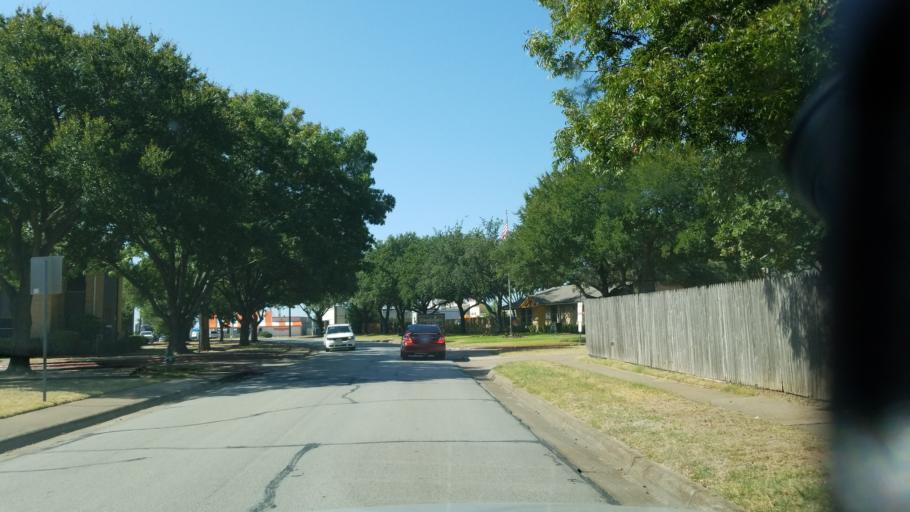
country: US
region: Texas
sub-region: Dallas County
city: Duncanville
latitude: 32.6353
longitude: -96.9008
